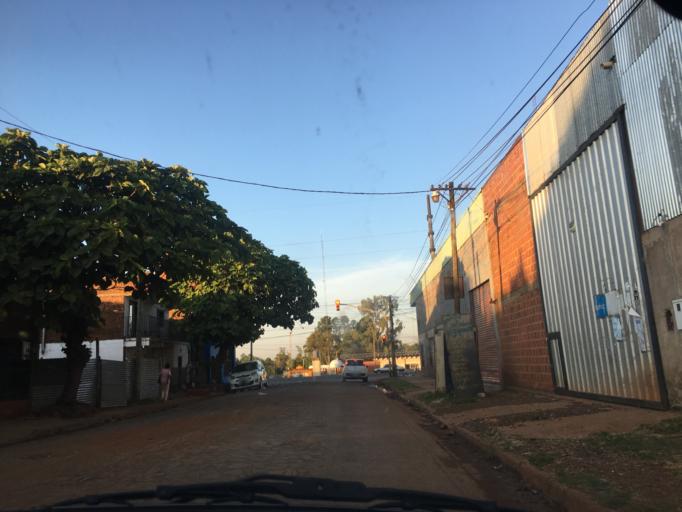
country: AR
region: Misiones
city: Garupa
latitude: -27.4436
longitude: -55.8737
